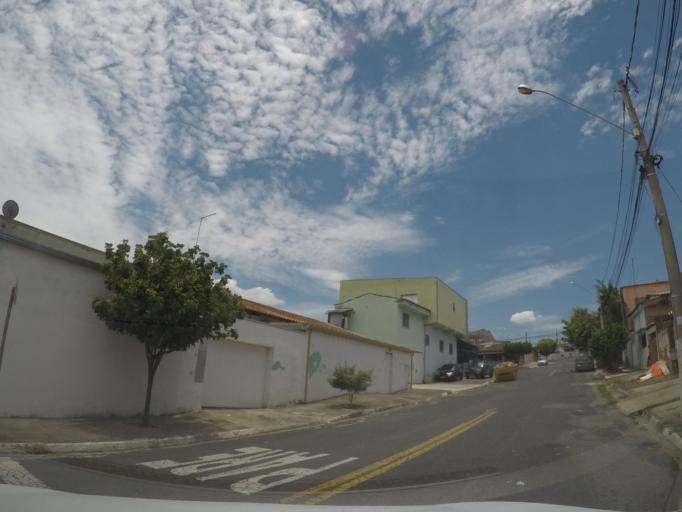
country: BR
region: Sao Paulo
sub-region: Hortolandia
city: Hortolandia
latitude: -22.8379
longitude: -47.1988
